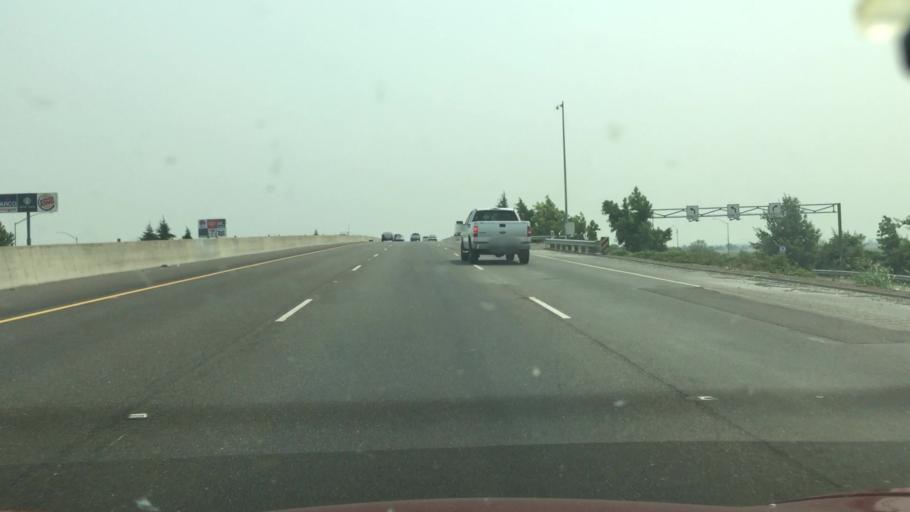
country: US
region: California
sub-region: San Joaquin County
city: Kennedy
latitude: 37.9067
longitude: -121.2238
